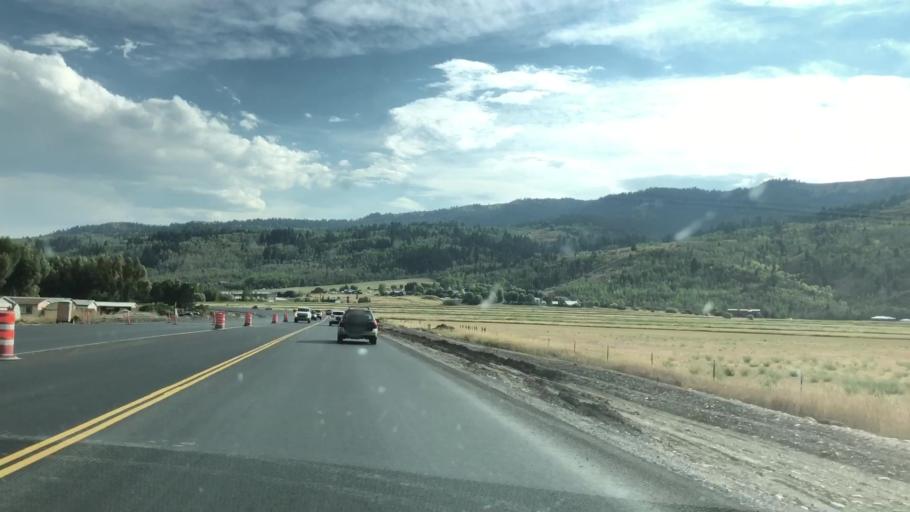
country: US
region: Wyoming
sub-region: Teton County
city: South Park
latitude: 43.3797
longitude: -110.7444
